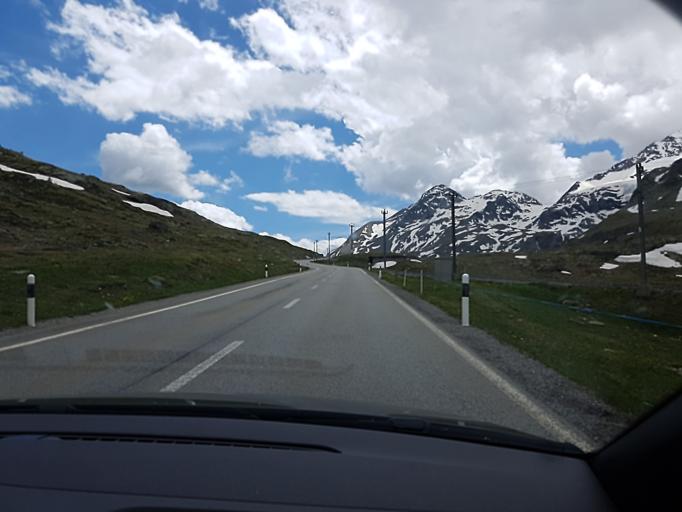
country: CH
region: Grisons
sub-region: Bernina District
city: Poschiavo
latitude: 46.4249
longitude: 10.0003
